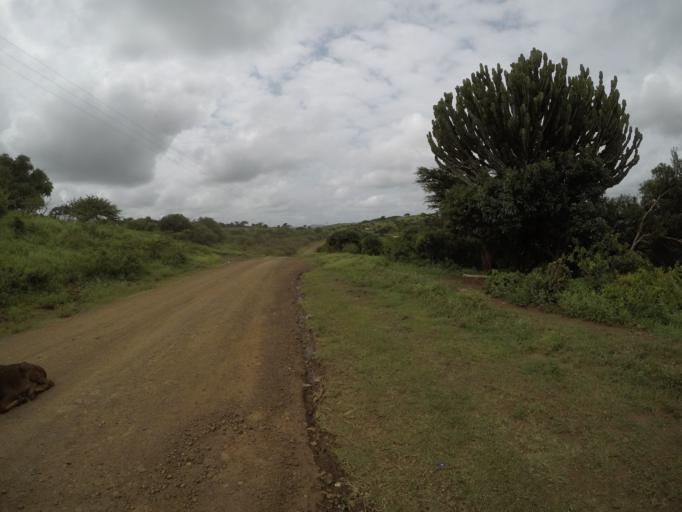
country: ZA
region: KwaZulu-Natal
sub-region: uThungulu District Municipality
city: Empangeni
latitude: -28.6104
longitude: 31.8973
